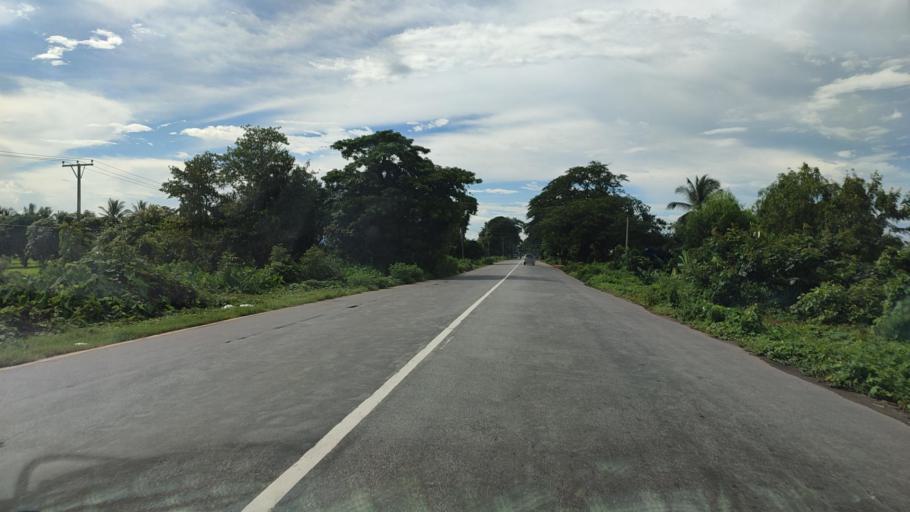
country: MM
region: Bago
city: Pyu
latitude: 18.3227
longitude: 96.4997
